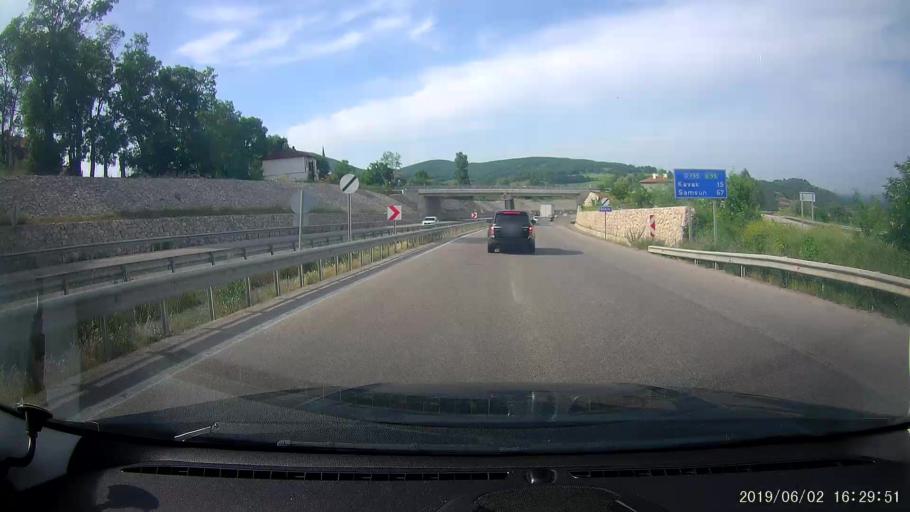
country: TR
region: Samsun
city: Ladik
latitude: 41.0187
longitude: 35.8727
